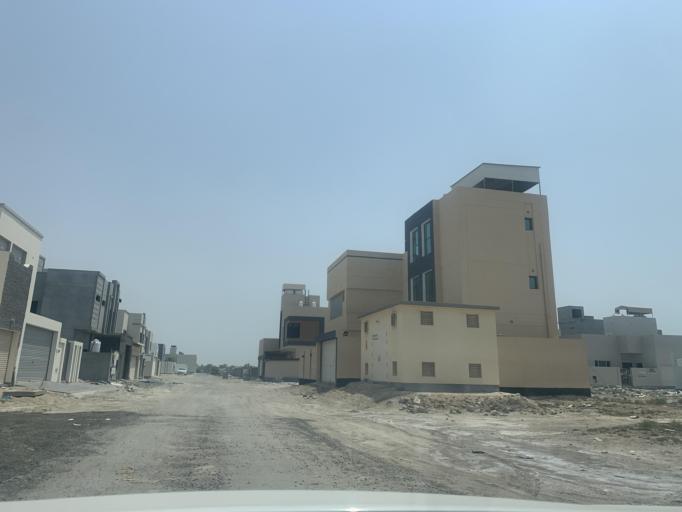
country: BH
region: Central Governorate
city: Madinat Hamad
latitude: 26.1309
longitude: 50.4667
